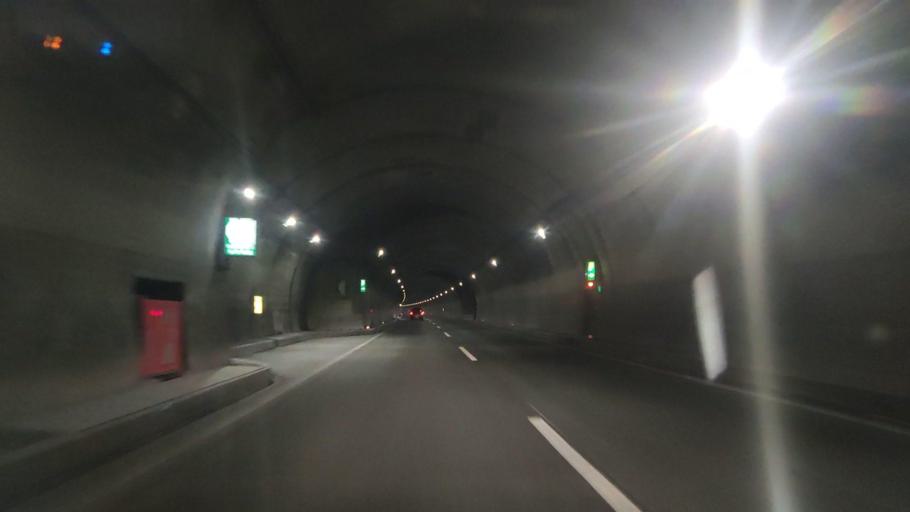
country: JP
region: Oita
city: Beppu
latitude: 33.2730
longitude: 131.3425
